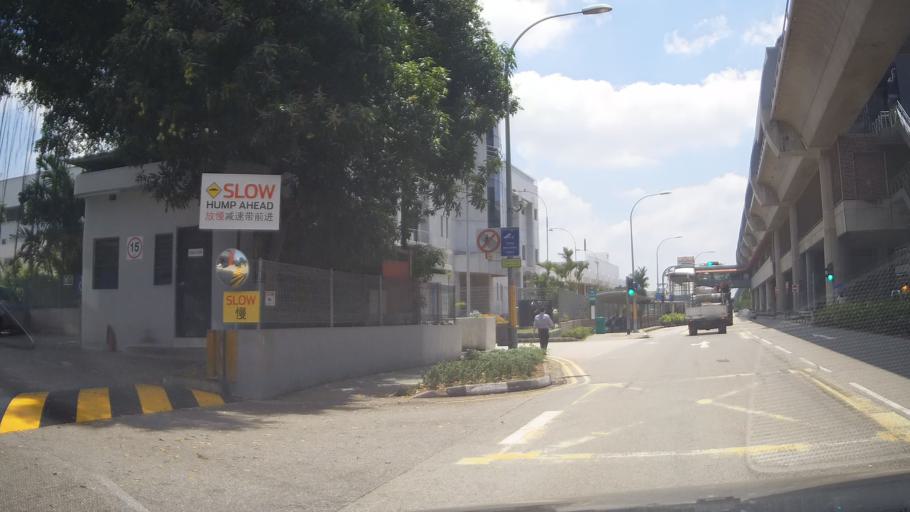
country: MY
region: Johor
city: Johor Bahru
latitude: 1.3279
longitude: 103.6772
